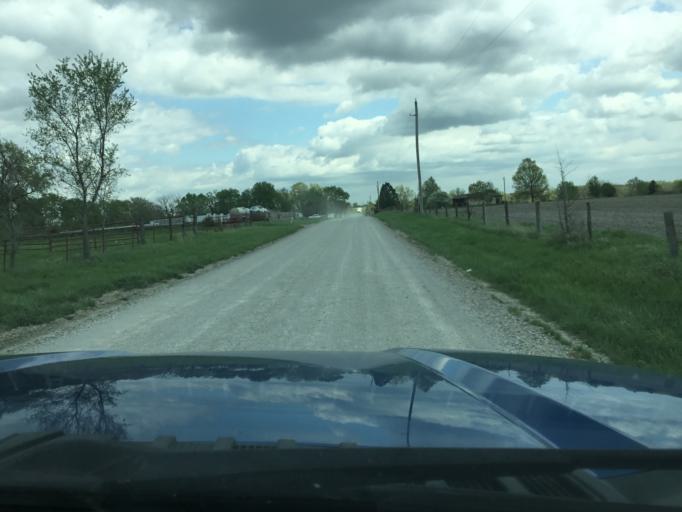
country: US
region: Kansas
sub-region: Douglas County
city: Eudora
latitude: 38.9278
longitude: -95.0870
